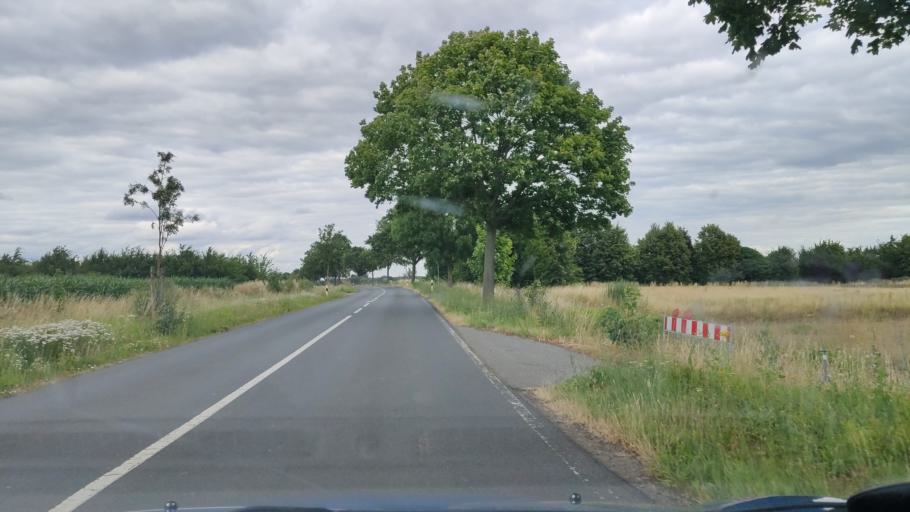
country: DE
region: Lower Saxony
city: Ronnenberg
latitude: 52.2964
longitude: 9.6454
